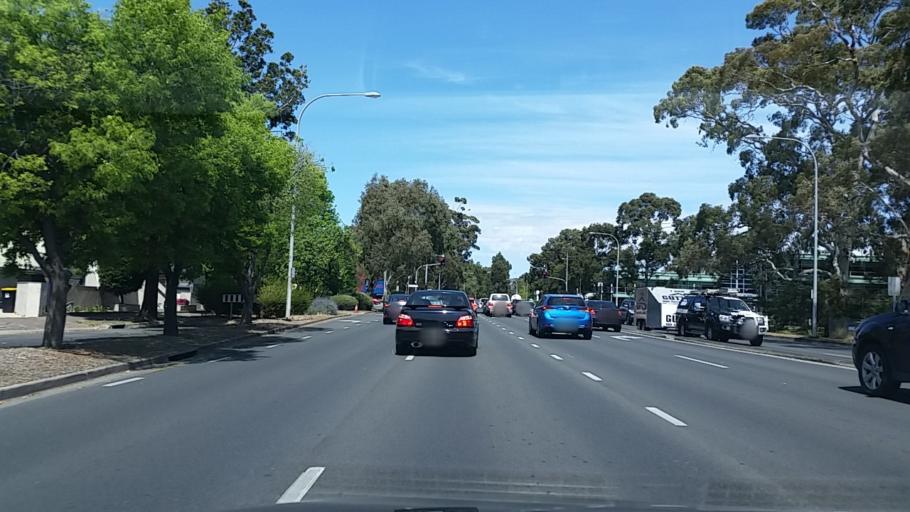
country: AU
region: South Australia
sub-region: Unley
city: Fullarton
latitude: -34.9391
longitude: 138.6244
